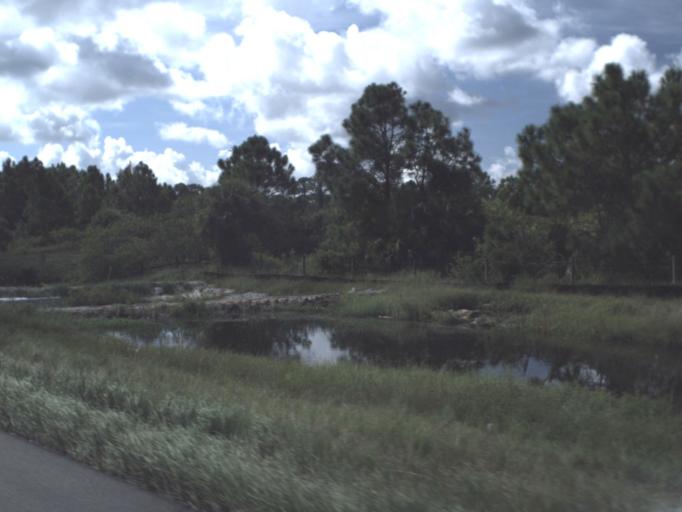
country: US
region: Florida
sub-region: Charlotte County
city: Port Charlotte
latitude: 27.0549
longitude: -82.0797
